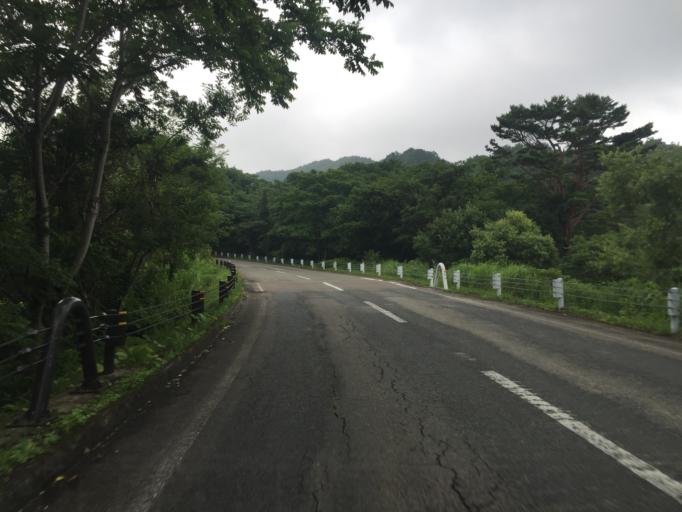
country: JP
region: Fukushima
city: Inawashiro
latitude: 37.6668
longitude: 140.1013
